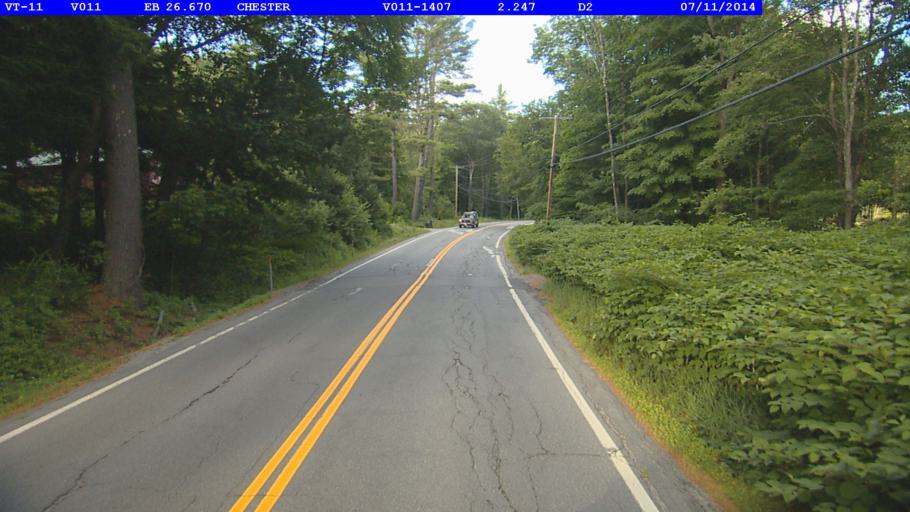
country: US
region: Vermont
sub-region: Windsor County
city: Chester
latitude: 43.2623
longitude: -72.6432
